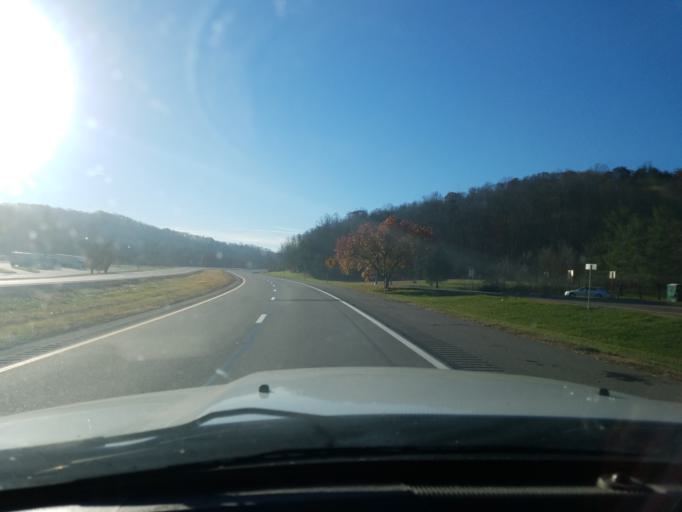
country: US
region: West Virginia
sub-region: Wood County
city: Mineral Wells
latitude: 39.1317
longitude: -81.5482
